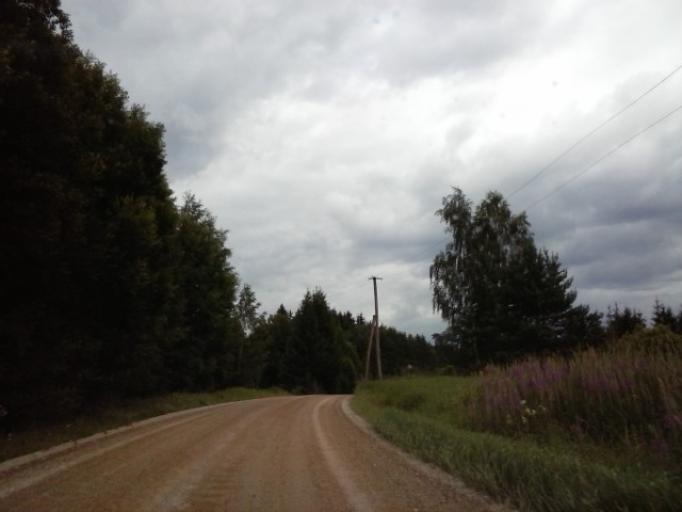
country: EE
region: Vorumaa
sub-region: Voru linn
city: Voru
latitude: 57.7476
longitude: 27.0721
